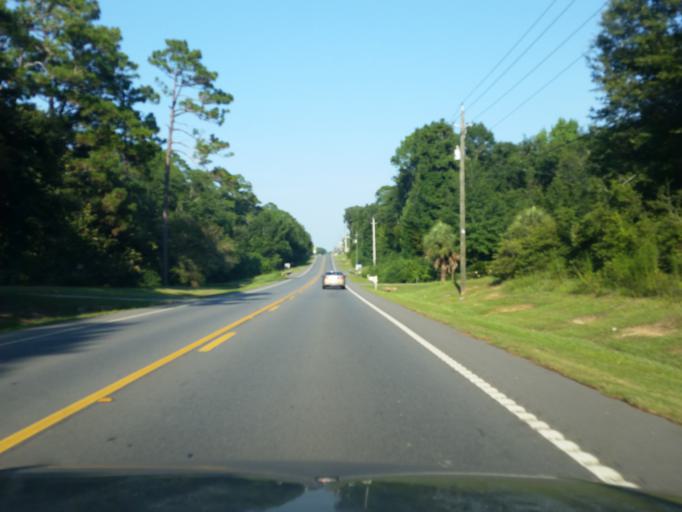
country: US
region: Alabama
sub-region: Baldwin County
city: Foley
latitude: 30.4068
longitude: -87.6576
